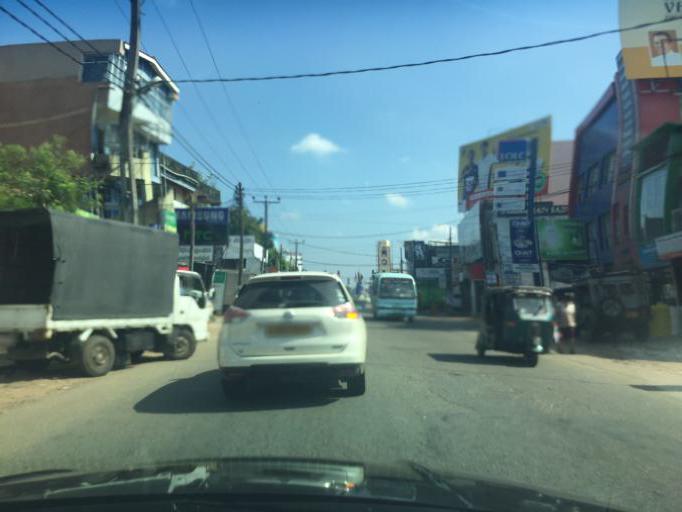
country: LK
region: Western
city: Maharagama
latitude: 6.8028
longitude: 79.9219
